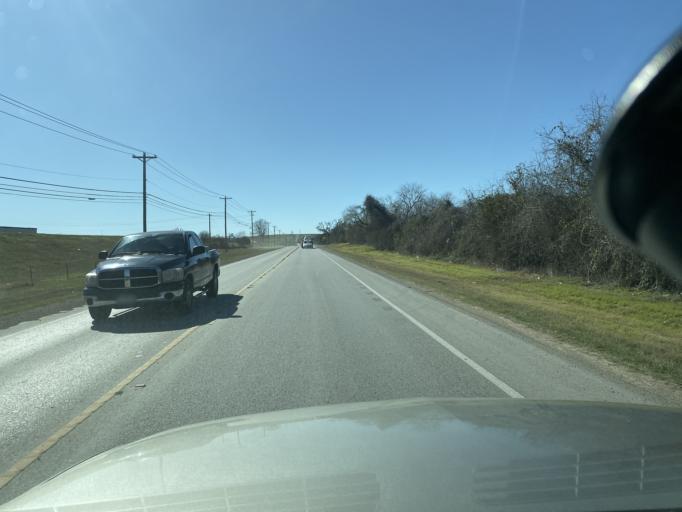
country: US
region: Texas
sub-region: Travis County
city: Garfield
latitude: 30.1713
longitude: -97.6540
